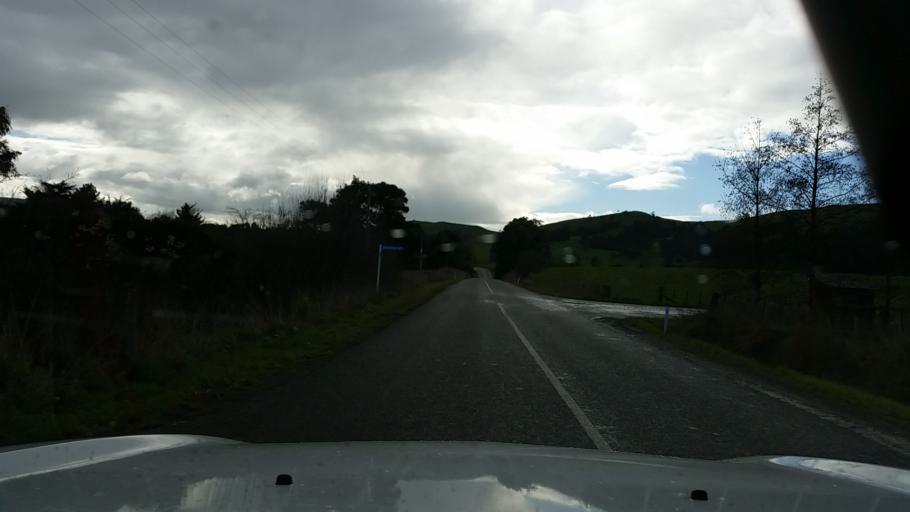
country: NZ
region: Wellington
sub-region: South Wairarapa District
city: Waipawa
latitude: -41.1903
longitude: 175.5865
